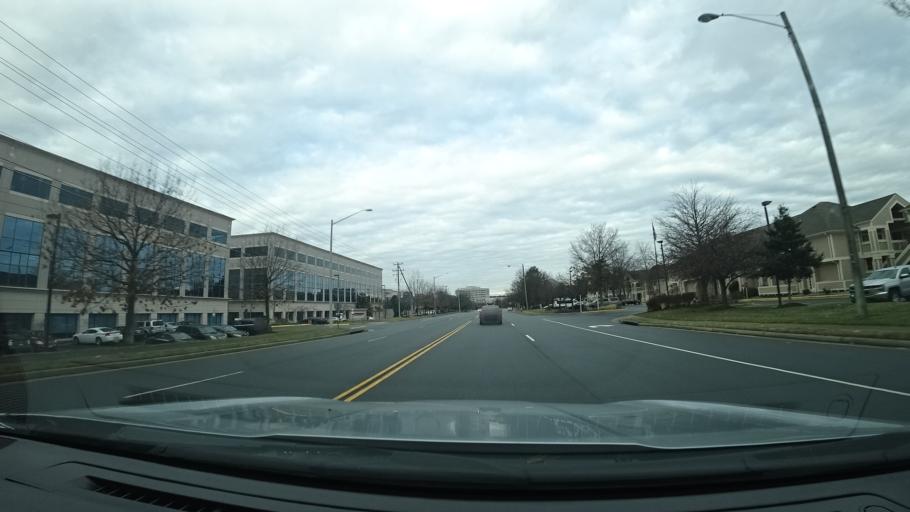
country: US
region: Virginia
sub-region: Fairfax County
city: Floris
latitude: 38.9510
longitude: -77.4207
